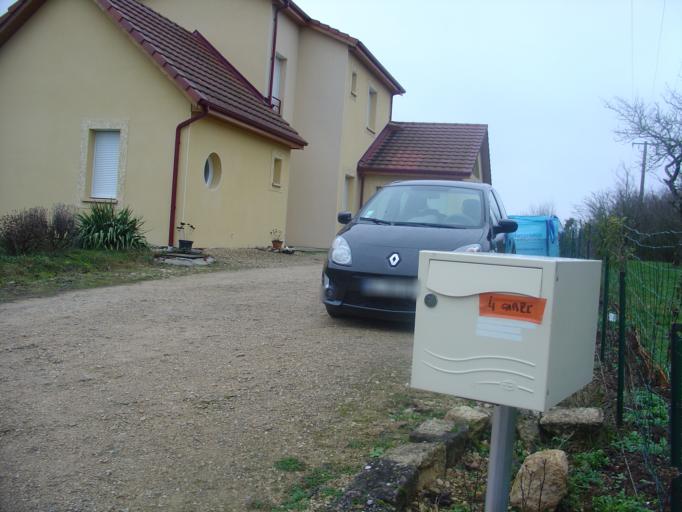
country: FR
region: Lorraine
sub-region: Departement de Meurthe-et-Moselle
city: Villey-Saint-Etienne
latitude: 48.8054
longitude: 5.9433
